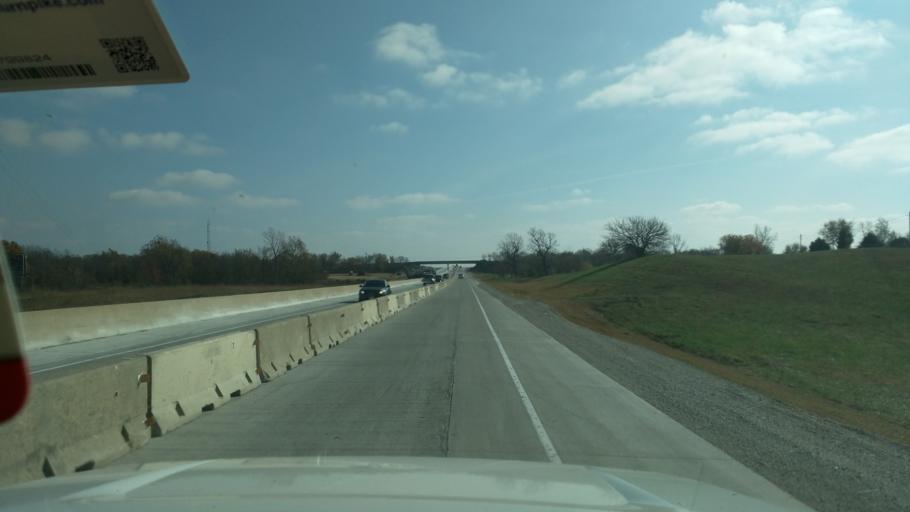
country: US
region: Oklahoma
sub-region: Wagoner County
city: Coweta
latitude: 36.0185
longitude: -95.6789
